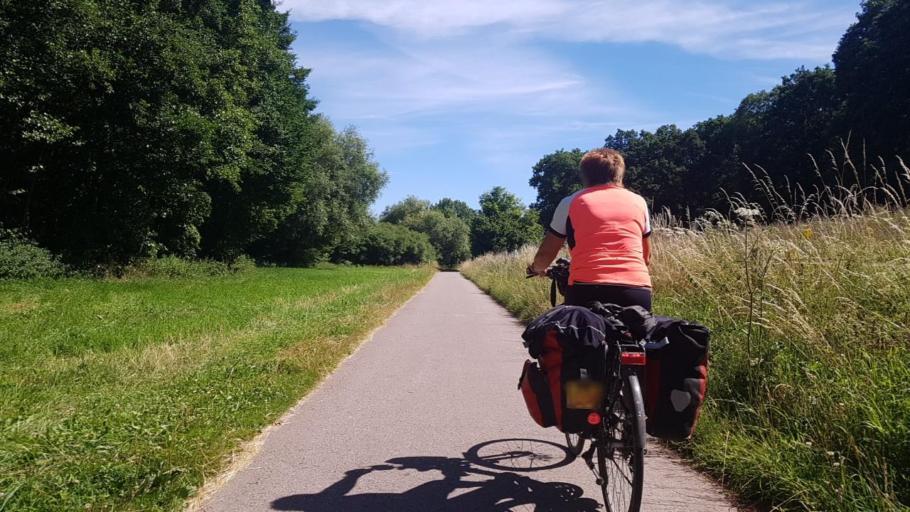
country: DE
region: North Rhine-Westphalia
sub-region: Regierungsbezirk Koln
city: Mechernich
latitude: 50.6235
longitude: 6.6688
